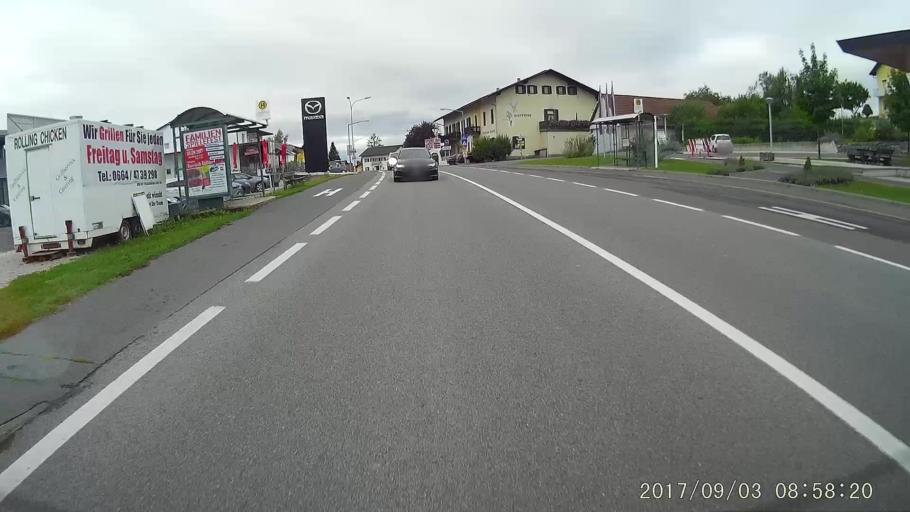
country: AT
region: Styria
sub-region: Politischer Bezirk Suedoststeiermark
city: Merkendorf
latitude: 46.8673
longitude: 15.9026
